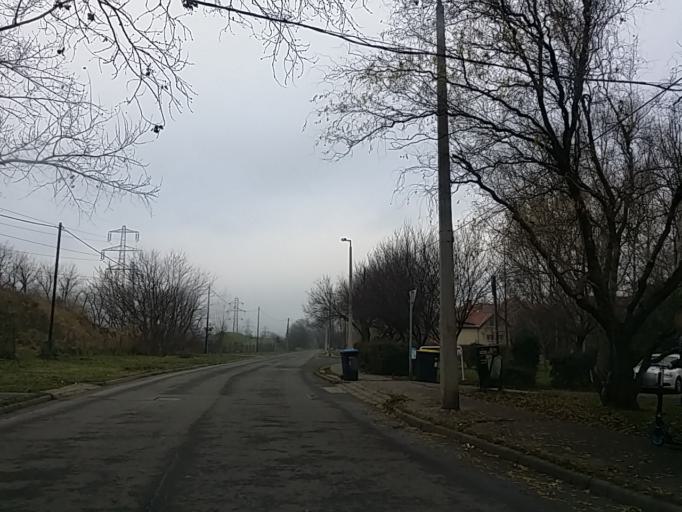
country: HU
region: Budapest
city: Budapest III. keruelet
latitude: 47.5660
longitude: 19.0569
